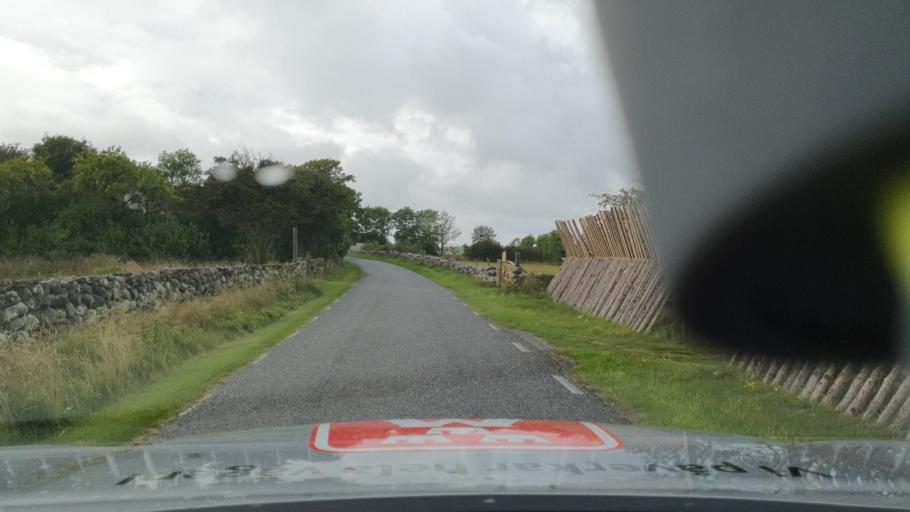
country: SE
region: Gotland
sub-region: Gotland
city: Hemse
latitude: 57.0026
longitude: 18.3442
